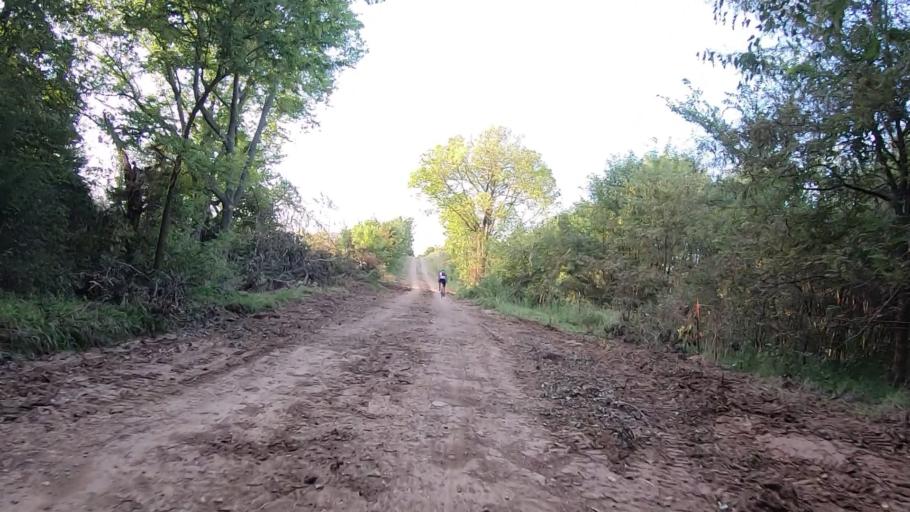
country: US
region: Kansas
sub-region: Marshall County
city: Blue Rapids
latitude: 39.7573
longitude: -96.7506
